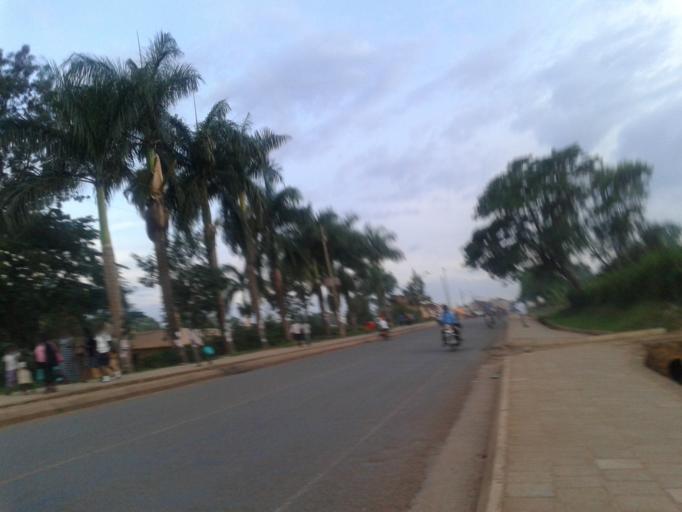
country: UG
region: Eastern Region
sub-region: Mbale District
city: Mbale
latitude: 1.0817
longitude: 34.1791
